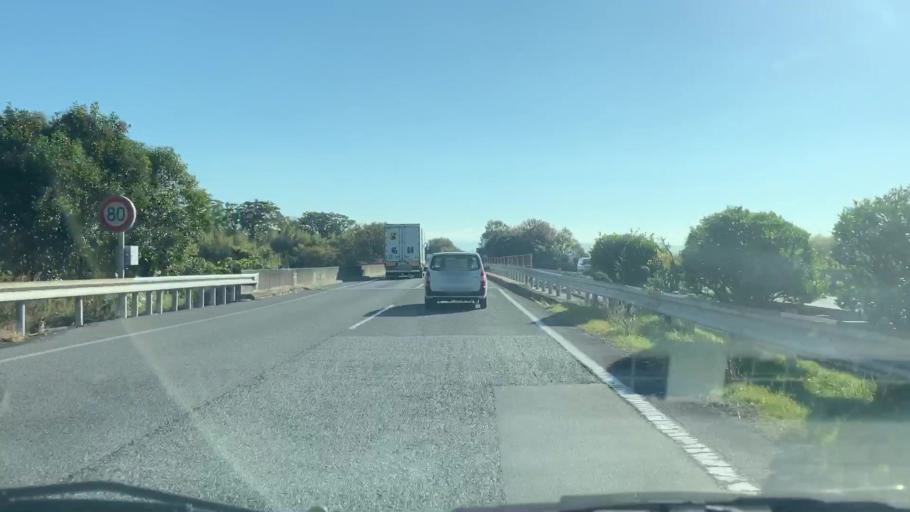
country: JP
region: Saga Prefecture
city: Saga-shi
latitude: 33.3077
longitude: 130.2273
